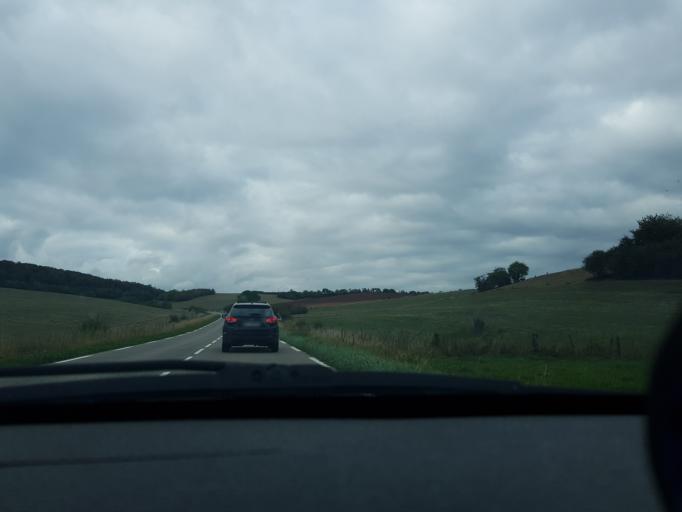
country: FR
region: Lorraine
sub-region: Departement de la Moselle
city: Chateau-Salins
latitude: 48.8787
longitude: 6.5363
